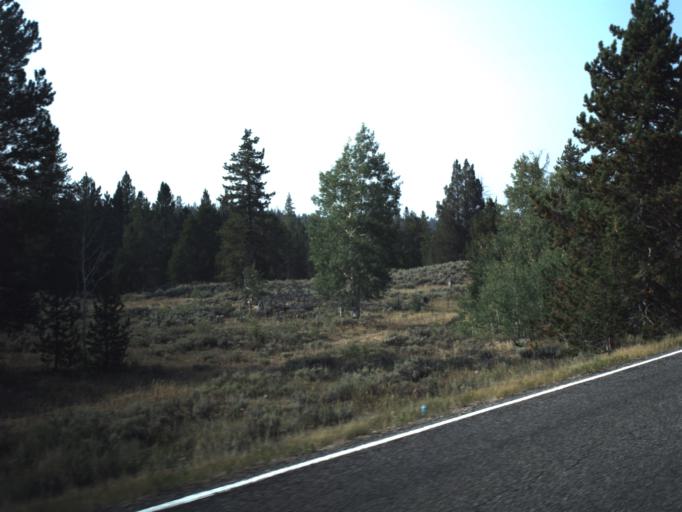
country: US
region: Wyoming
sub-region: Uinta County
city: Evanston
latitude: 40.8916
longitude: -110.8314
